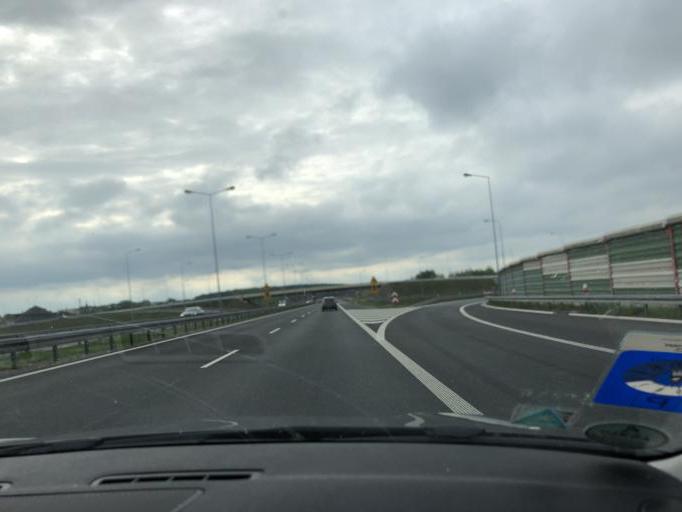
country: PL
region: Opole Voivodeship
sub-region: Powiat krapkowicki
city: Gogolin
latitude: 50.4868
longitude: 17.9964
